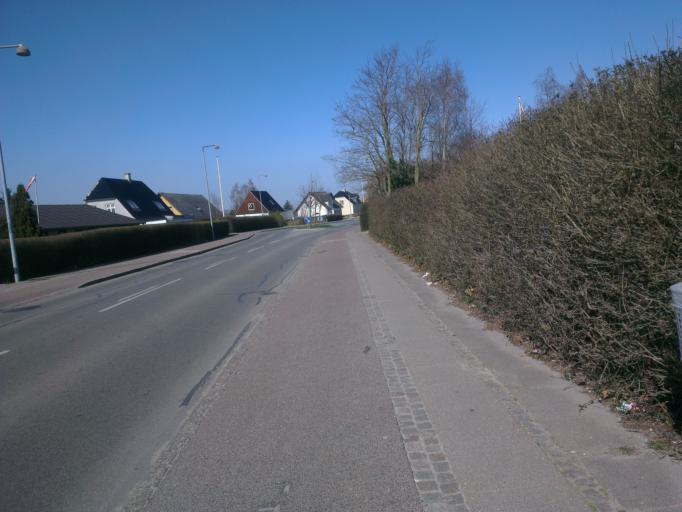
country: DK
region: Capital Region
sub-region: Frederikssund Kommune
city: Frederikssund
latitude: 55.8528
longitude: 12.0633
